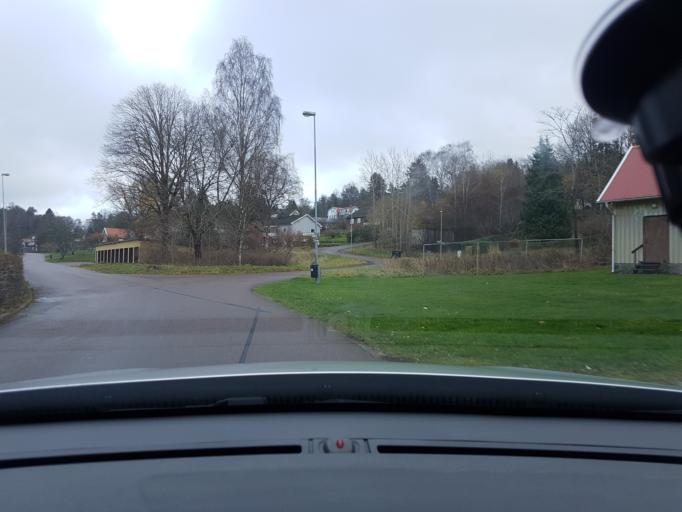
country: SE
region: Vaestra Goetaland
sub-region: Ale Kommun
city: Alafors
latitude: 57.9177
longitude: 12.0716
